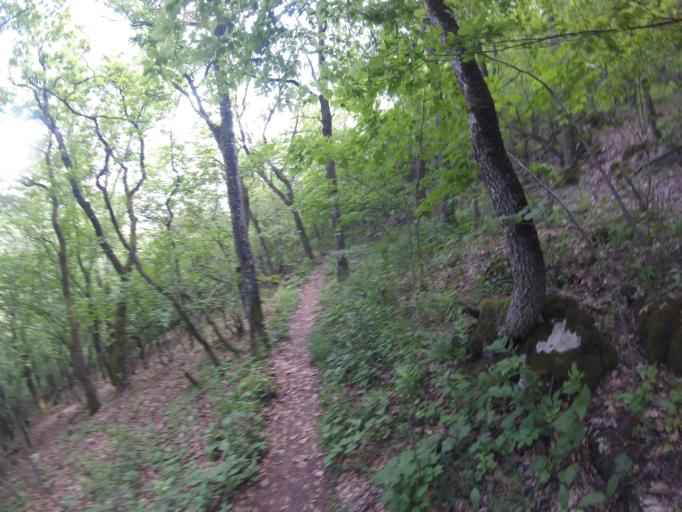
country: SK
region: Kosicky
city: Medzev
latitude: 48.6160
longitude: 20.8631
